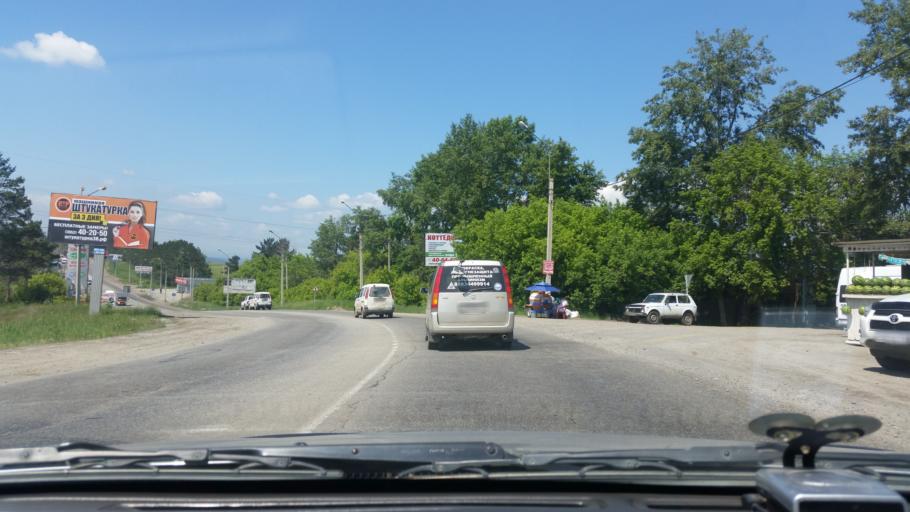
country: RU
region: Irkutsk
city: Smolenshchina
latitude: 52.2614
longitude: 104.1941
